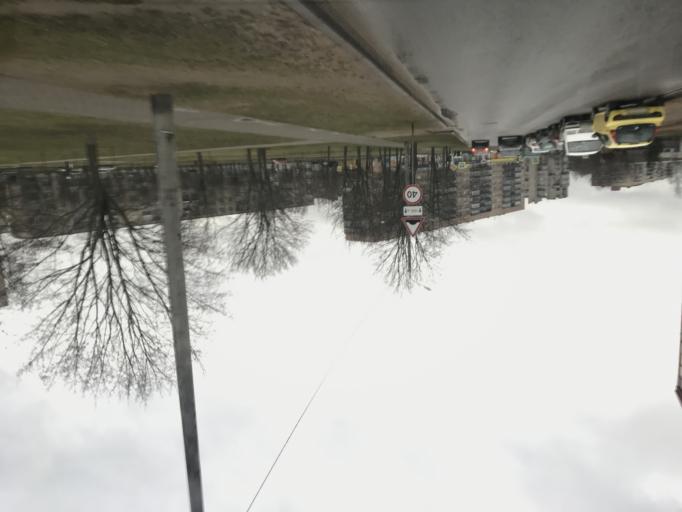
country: BY
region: Mogilev
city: Mahilyow
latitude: 53.8795
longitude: 30.3260
